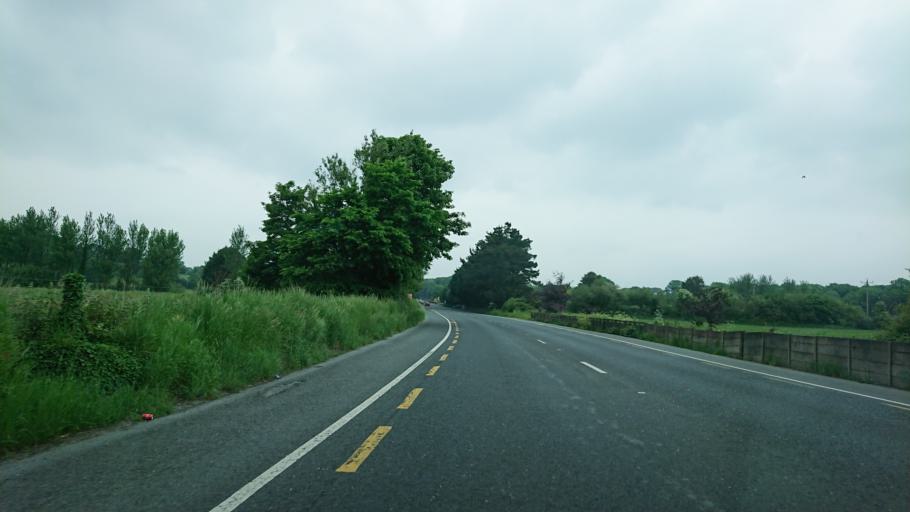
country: IE
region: Munster
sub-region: Waterford
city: Tra Mhor
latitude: 52.2035
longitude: -7.1163
